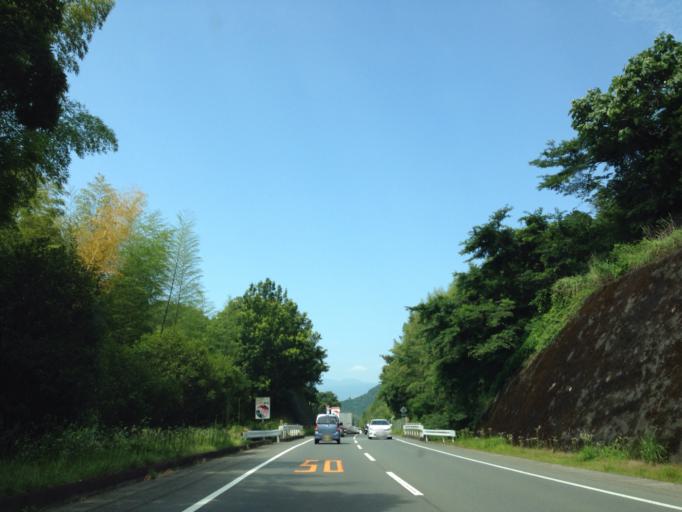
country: JP
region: Shizuoka
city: Mishima
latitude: 35.0478
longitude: 138.9215
